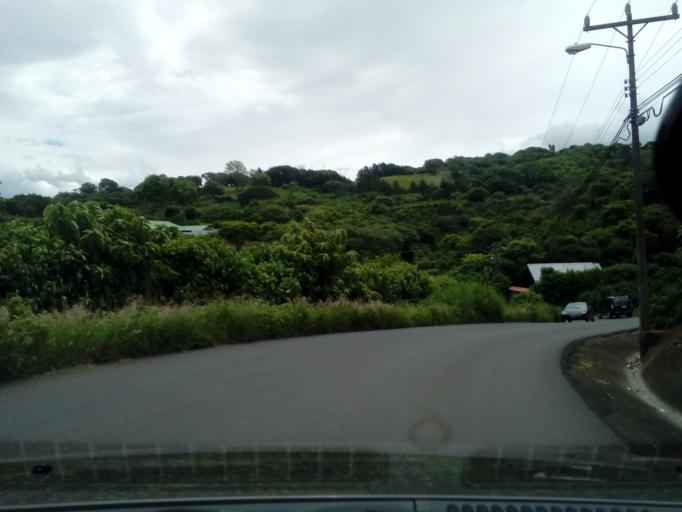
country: CR
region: Heredia
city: San Josecito
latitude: 10.0200
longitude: -84.0884
